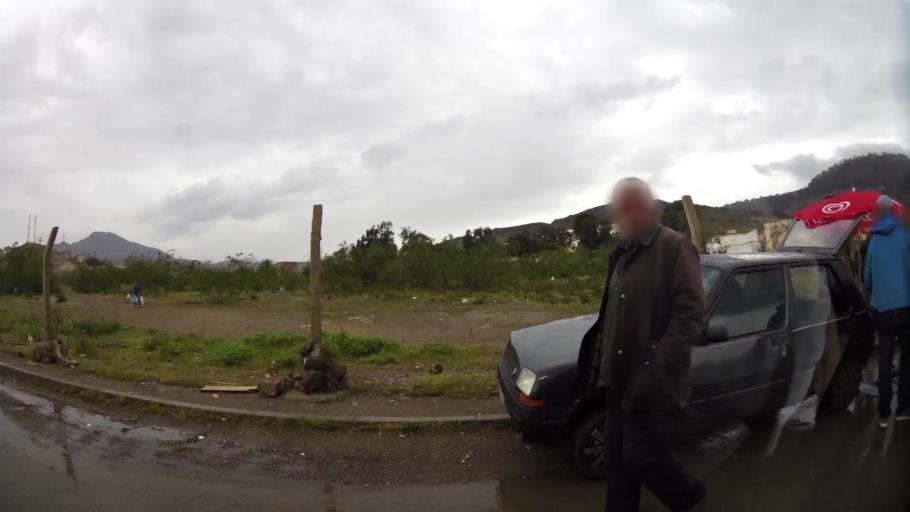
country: MA
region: Oriental
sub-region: Nador
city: Nador
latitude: 35.1493
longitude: -3.0049
